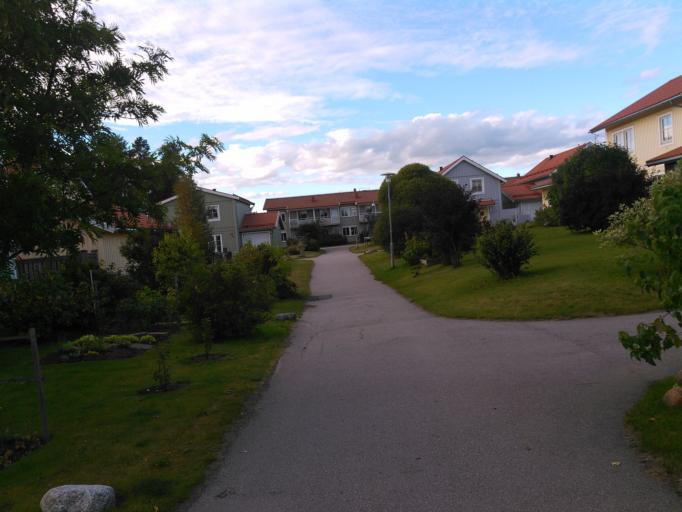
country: SE
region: Vaesterbotten
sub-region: Umea Kommun
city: Ersmark
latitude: 63.8058
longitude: 20.3403
